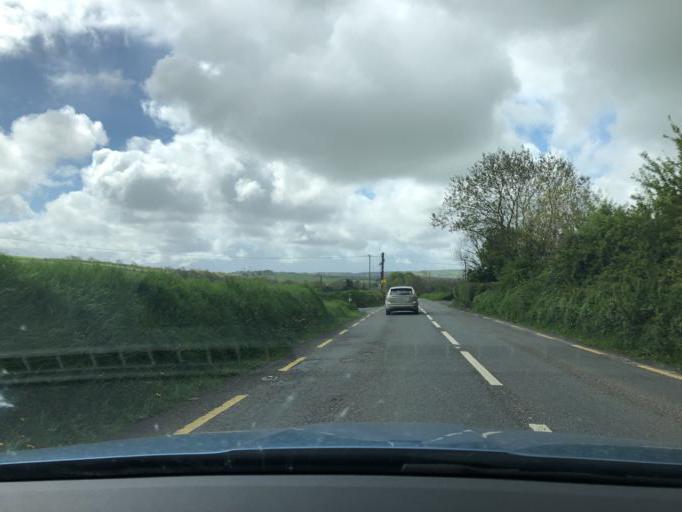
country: IE
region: Munster
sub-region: Ciarrai
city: Listowel
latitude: 52.4261
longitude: -9.5053
